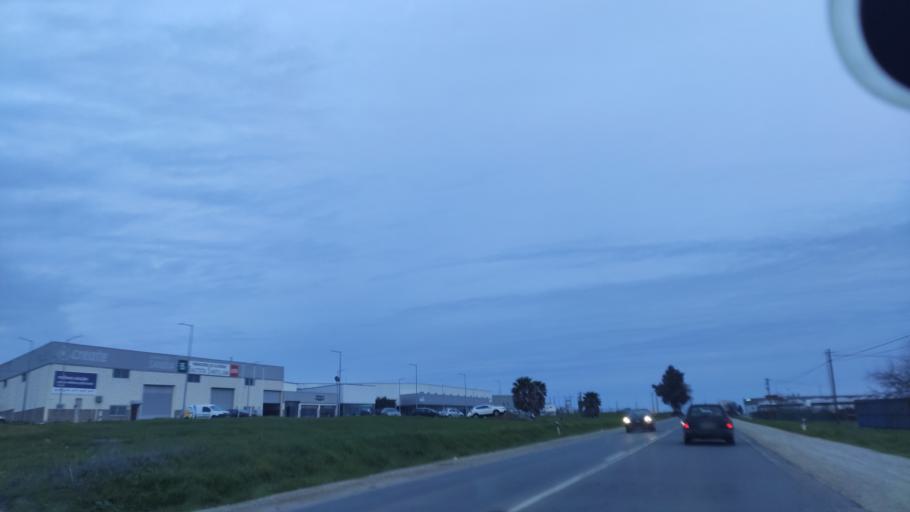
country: PT
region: Beja
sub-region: Beja
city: Beja
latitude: 38.0223
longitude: -7.8531
